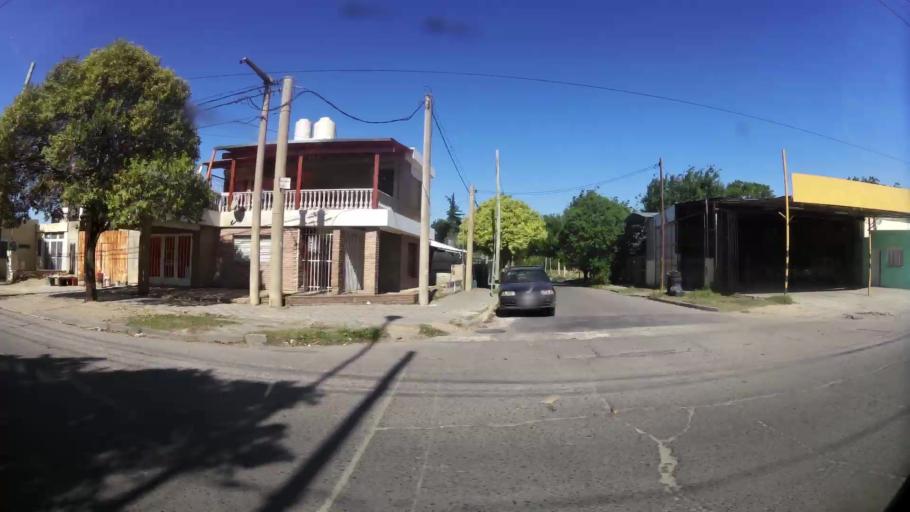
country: AR
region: Cordoba
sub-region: Departamento de Capital
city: Cordoba
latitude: -31.3756
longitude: -64.1838
